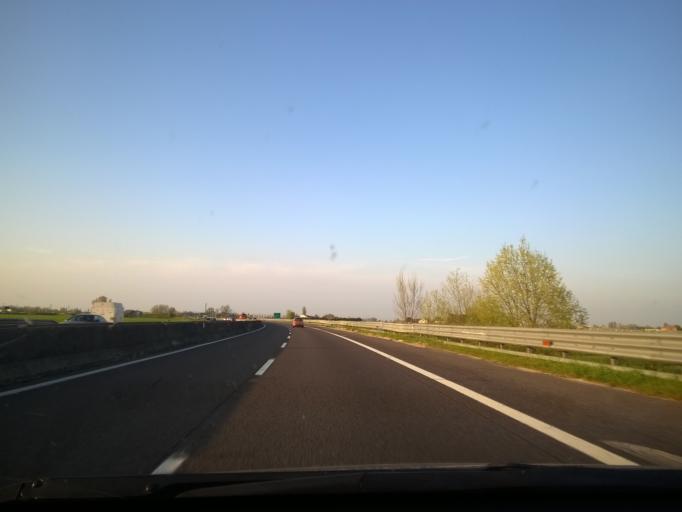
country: IT
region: Emilia-Romagna
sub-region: Provincia di Ferrara
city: San Martino
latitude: 44.7853
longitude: 11.5518
